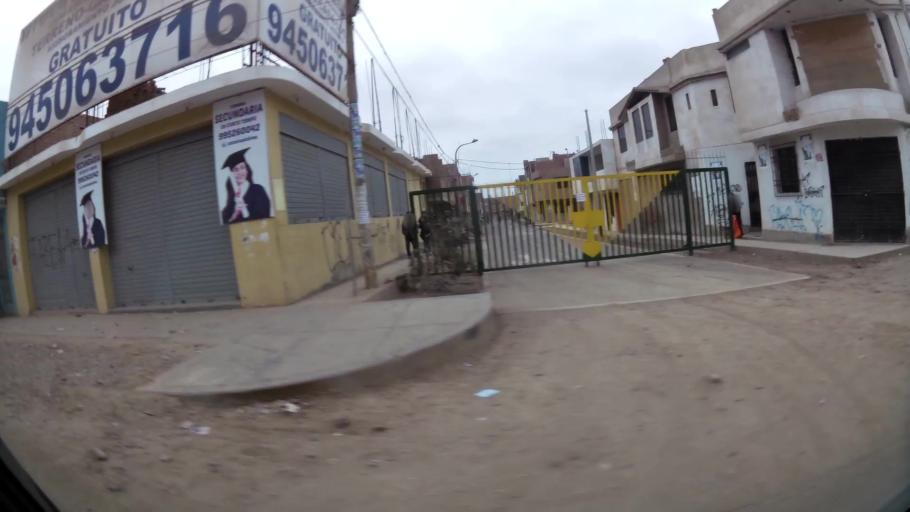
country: PE
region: Lima
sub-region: Lima
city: Independencia
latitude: -11.9610
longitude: -77.0954
